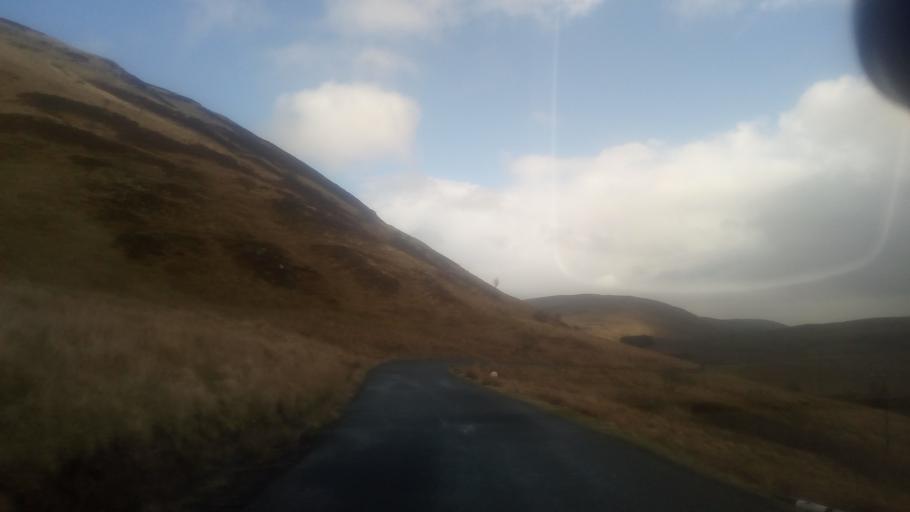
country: GB
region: Scotland
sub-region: The Scottish Borders
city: Innerleithen
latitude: 55.4641
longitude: -3.1260
